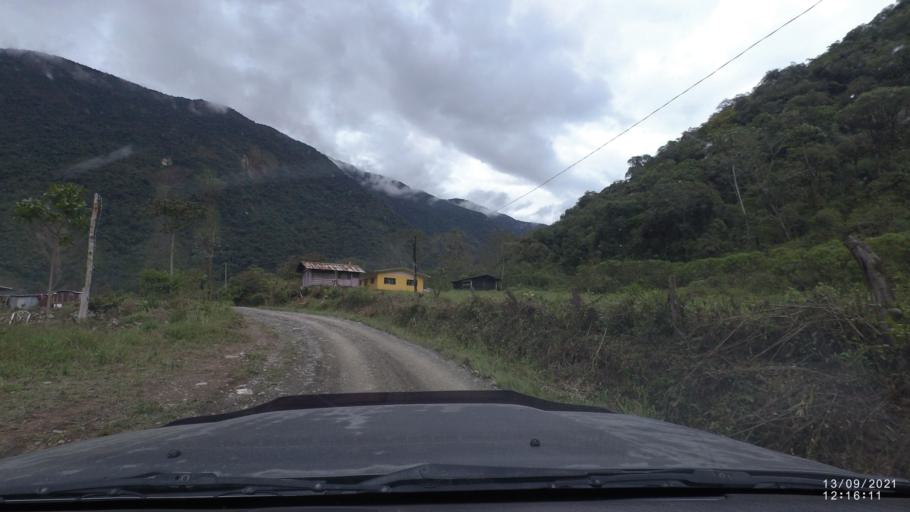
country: BO
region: Cochabamba
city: Colomi
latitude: -17.2245
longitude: -65.8204
